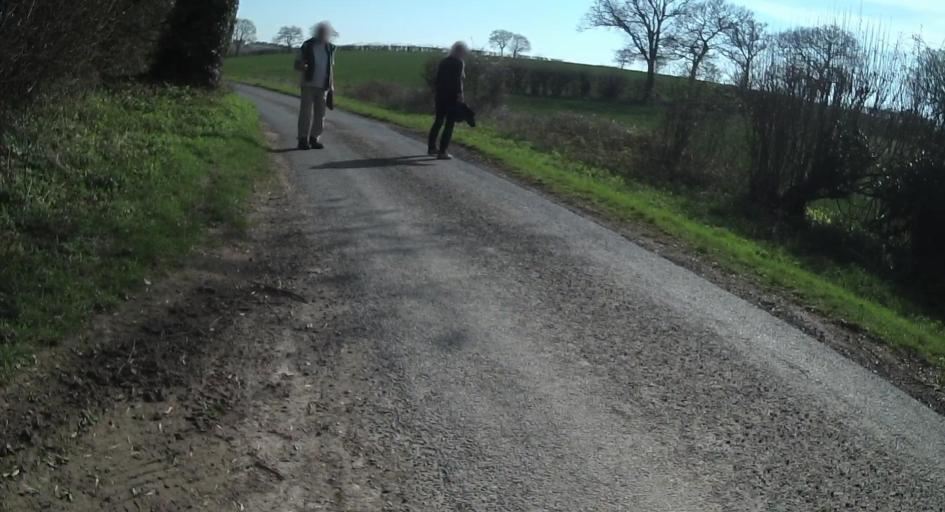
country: GB
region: England
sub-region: Hampshire
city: Highclere
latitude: 51.2698
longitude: -1.3906
